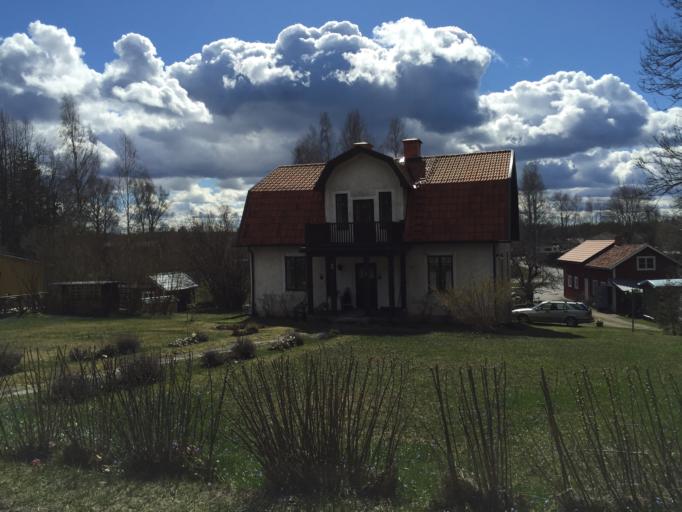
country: SE
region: OEstergoetland
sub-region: Norrkopings Kommun
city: Svartinge
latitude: 58.8276
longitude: 15.9385
